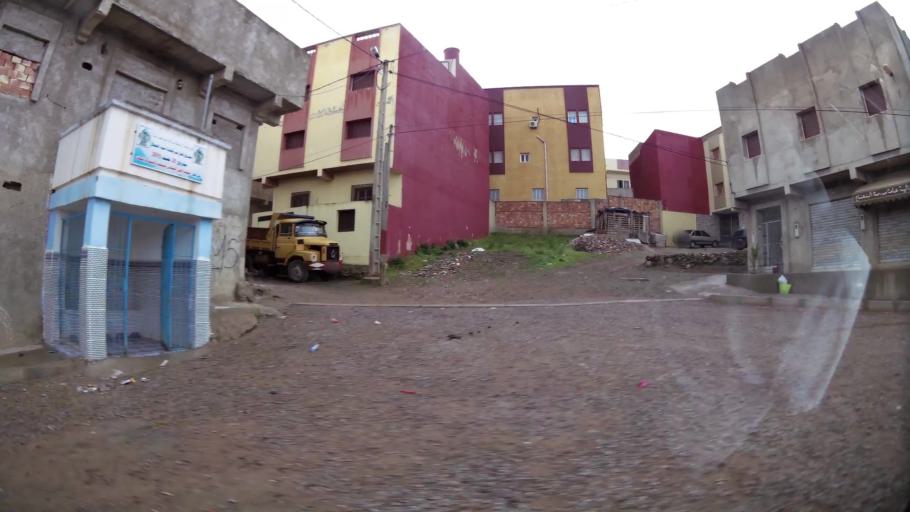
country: MA
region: Oriental
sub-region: Nador
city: Nador
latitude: 35.1486
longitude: -2.9854
